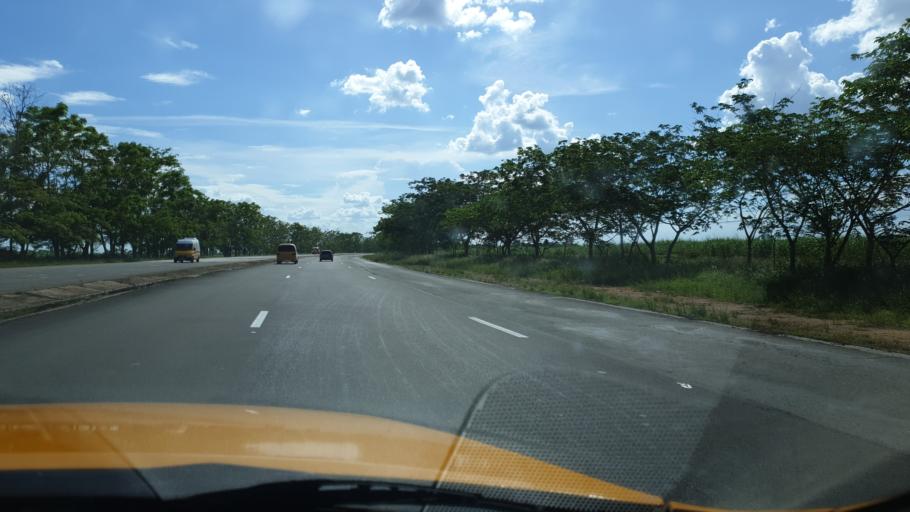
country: CU
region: Cienfuegos
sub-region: Municipio de Aguada de Pasajeros
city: Aguada de Pasajeros
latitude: 22.4022
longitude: -80.8503
